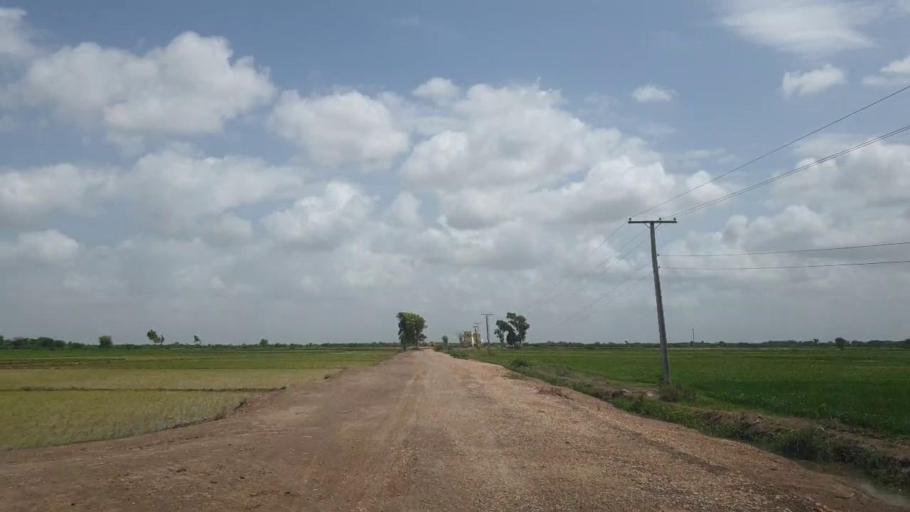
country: PK
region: Sindh
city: Tando Bago
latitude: 24.6493
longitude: 68.9934
